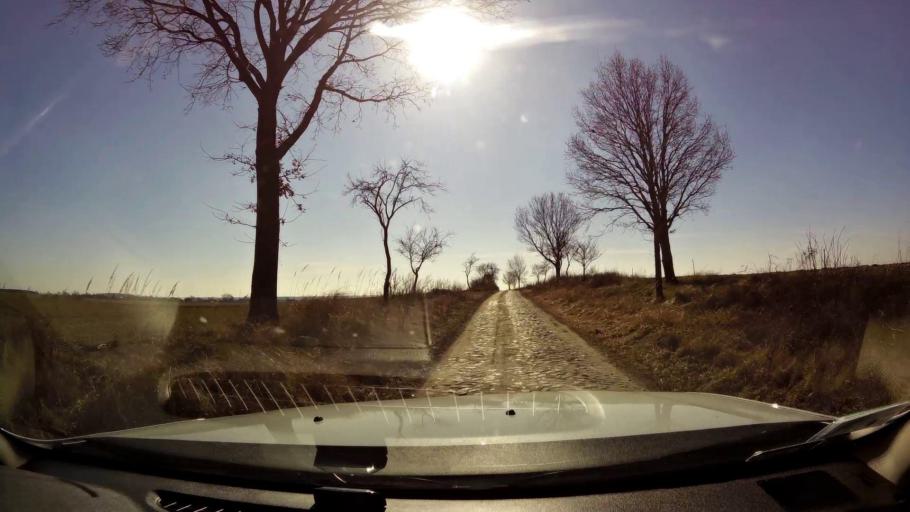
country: PL
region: West Pomeranian Voivodeship
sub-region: Powiat gryfinski
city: Banie
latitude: 53.1482
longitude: 14.6347
